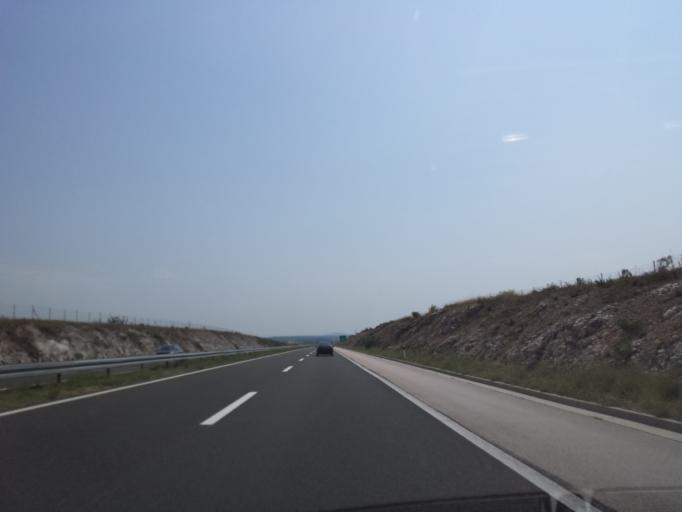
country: HR
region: Zadarska
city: Polaca
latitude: 44.0733
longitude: 15.5167
